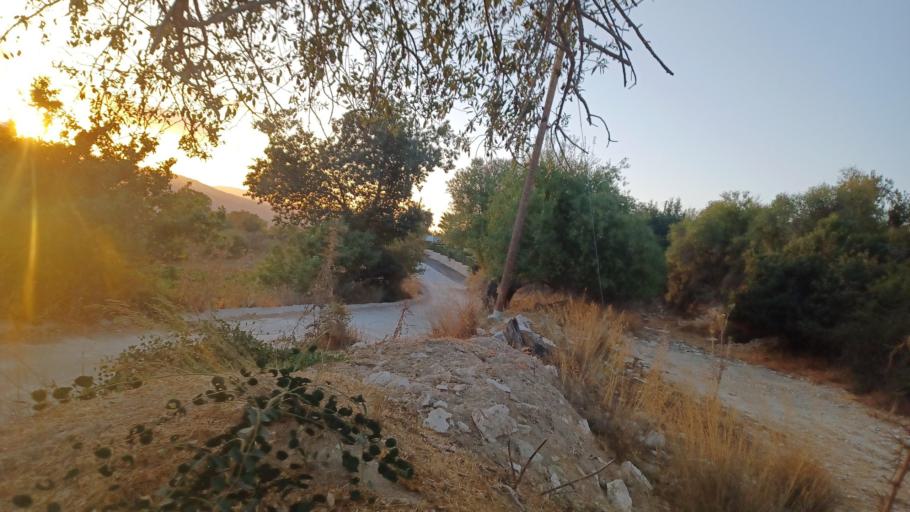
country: CY
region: Pafos
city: Mesogi
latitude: 34.8486
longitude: 32.5254
